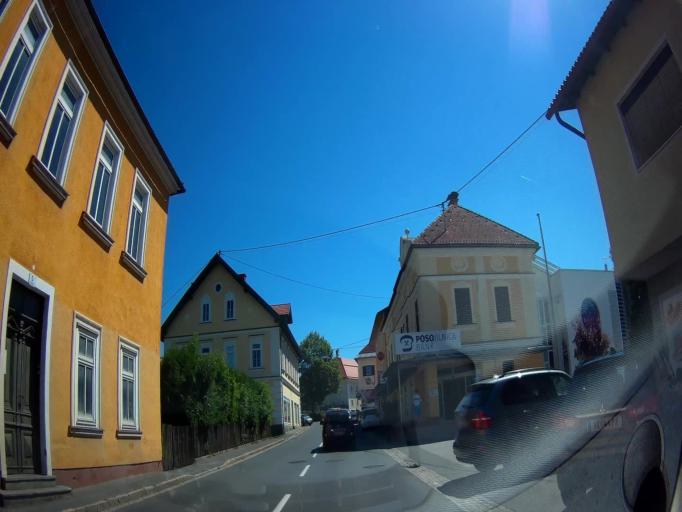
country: AT
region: Carinthia
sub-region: Politischer Bezirk Volkermarkt
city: Eberndorf
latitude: 46.5903
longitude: 14.6398
